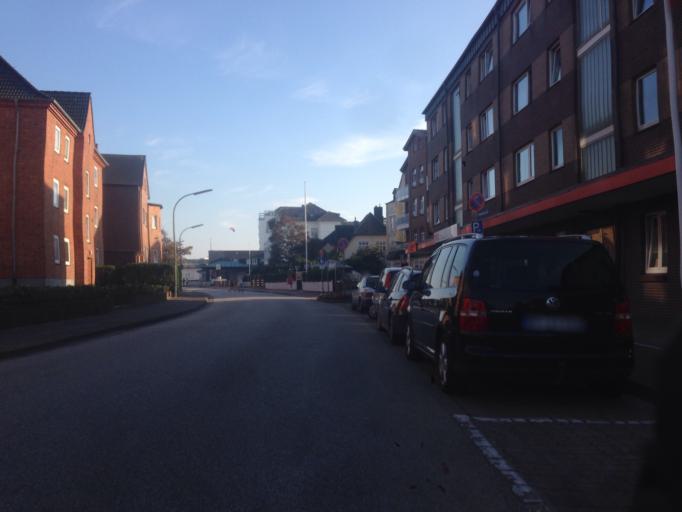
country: DE
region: Schleswig-Holstein
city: Westerland
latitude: 54.9109
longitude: 8.3050
